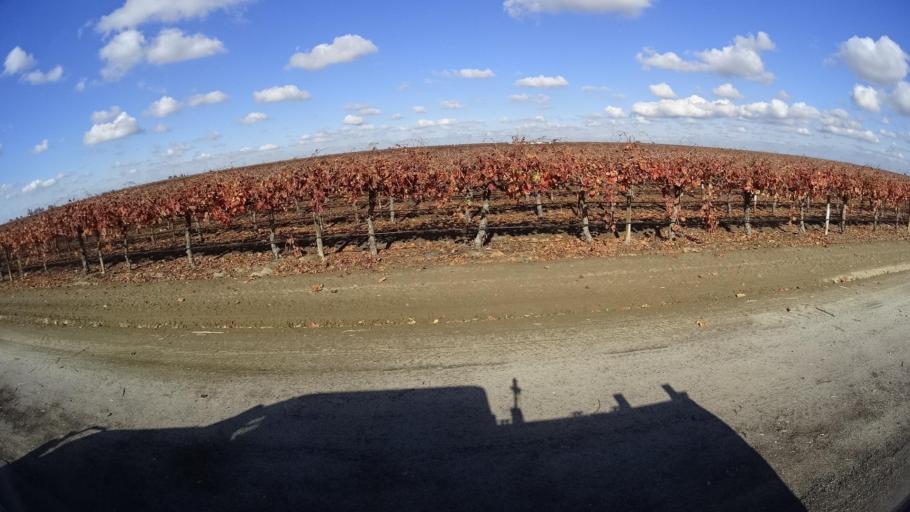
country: US
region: California
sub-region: Kern County
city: Delano
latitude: 35.7322
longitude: -119.3268
